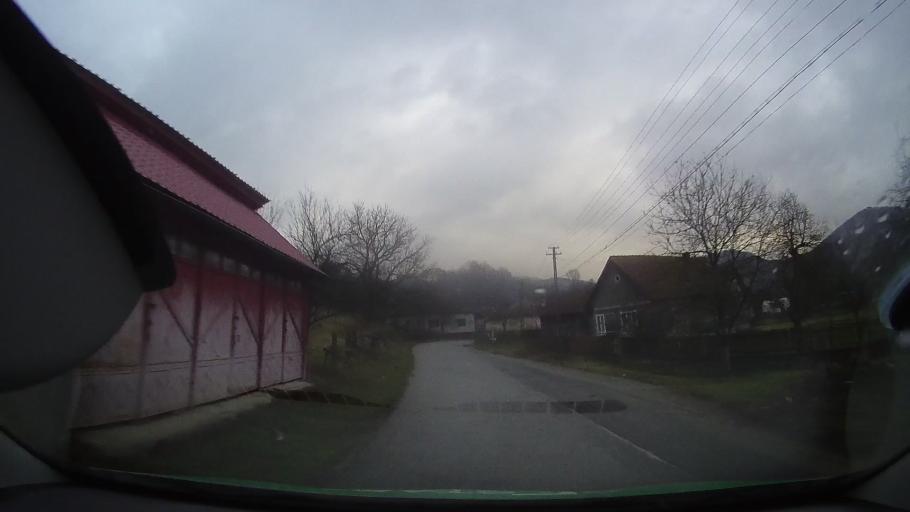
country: RO
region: Hunedoara
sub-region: Comuna Ribita
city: Ribita
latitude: 46.2276
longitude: 22.7284
